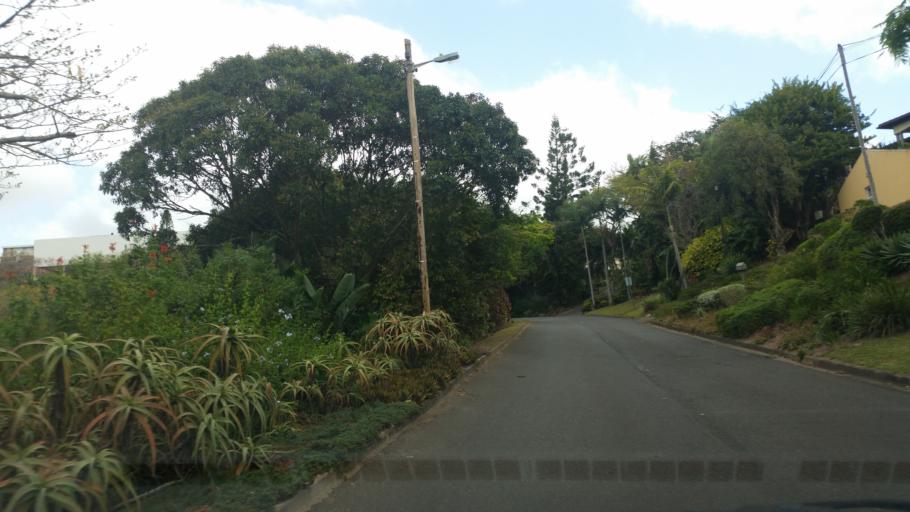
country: ZA
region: KwaZulu-Natal
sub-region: eThekwini Metropolitan Municipality
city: Berea
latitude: -29.8246
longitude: 30.9302
